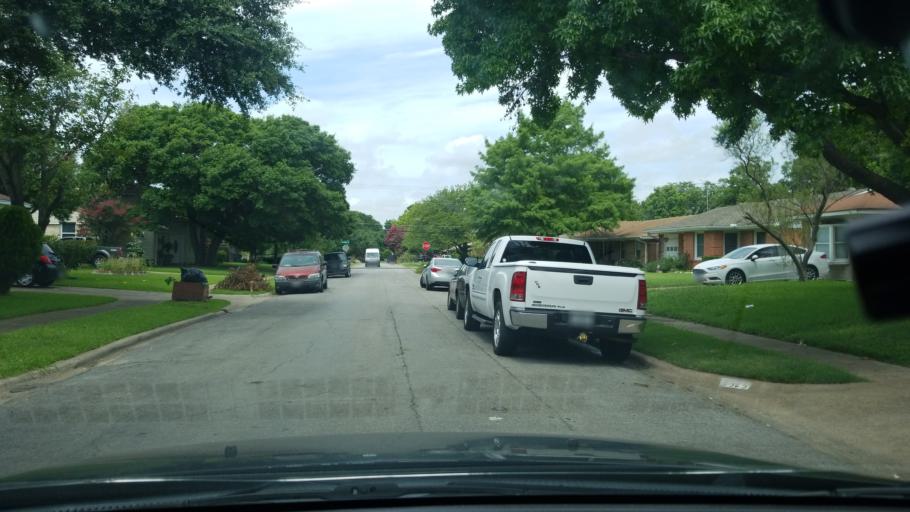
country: US
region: Texas
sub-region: Dallas County
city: Mesquite
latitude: 32.8169
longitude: -96.6722
